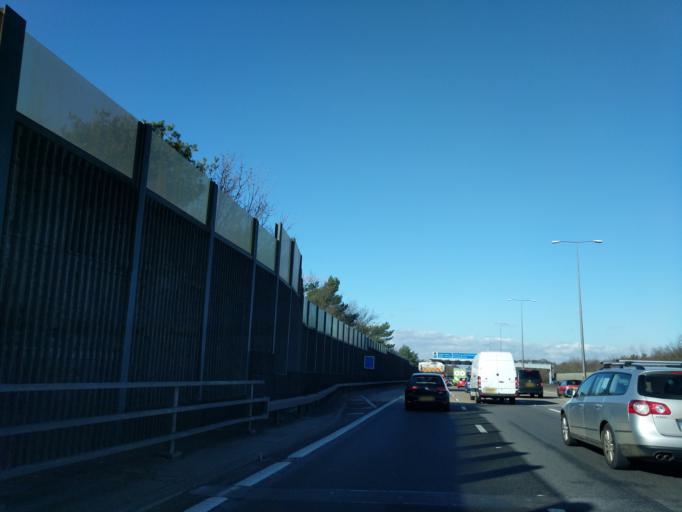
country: GB
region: England
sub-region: Surrey
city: Addlestone
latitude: 51.3532
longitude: -0.4907
